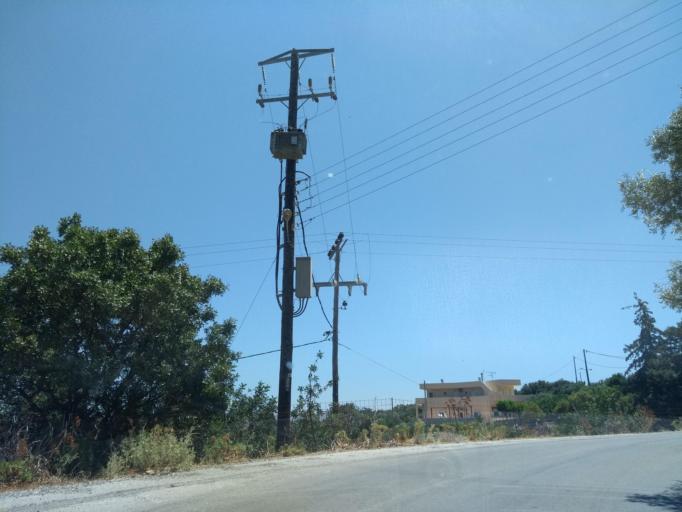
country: GR
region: Crete
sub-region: Nomos Chanias
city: Georgioupolis
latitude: 35.3166
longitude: 24.2909
